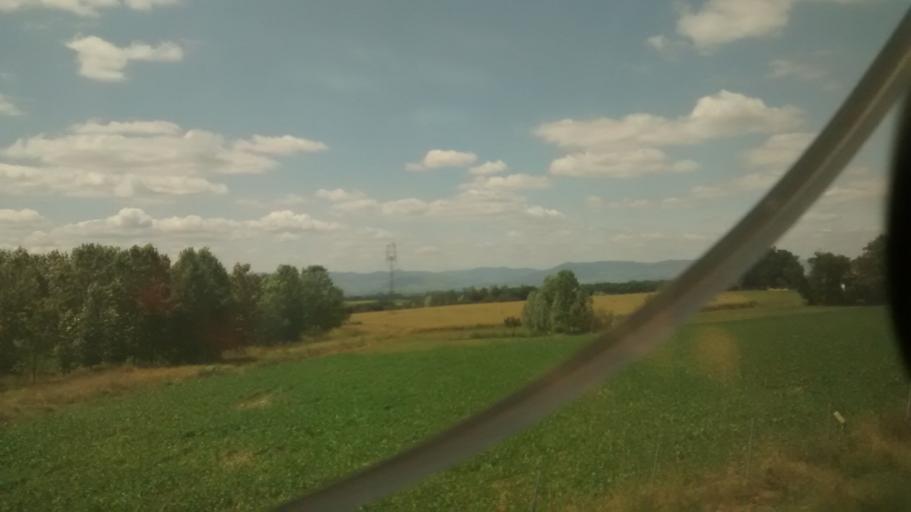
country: FR
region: Rhone-Alpes
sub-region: Departement de l'Ain
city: Villeneuve
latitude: 46.0346
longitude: 4.8504
